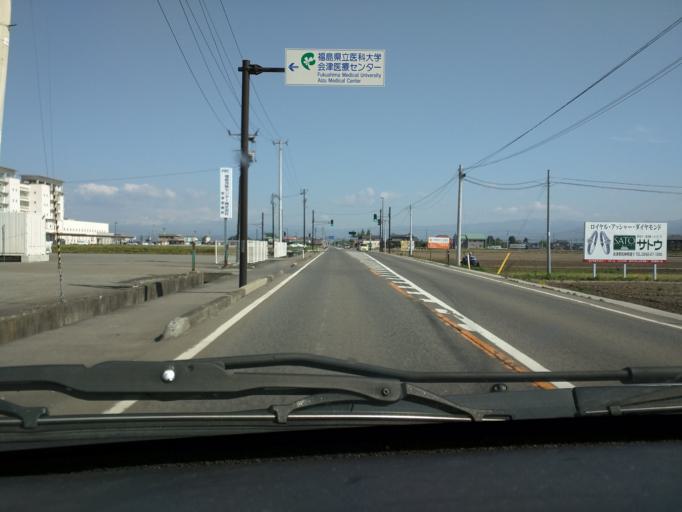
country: JP
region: Fukushima
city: Kitakata
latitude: 37.5507
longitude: 139.9099
